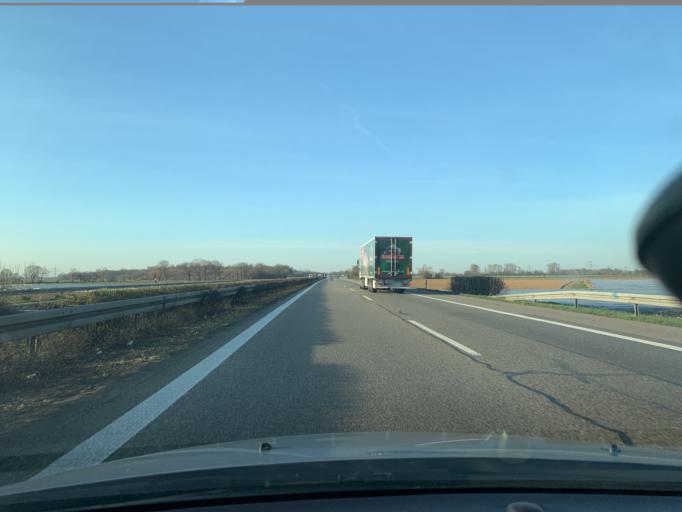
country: DE
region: Baden-Wuerttemberg
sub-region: Freiburg Region
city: Kenzingen
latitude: 48.1896
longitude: 7.7467
